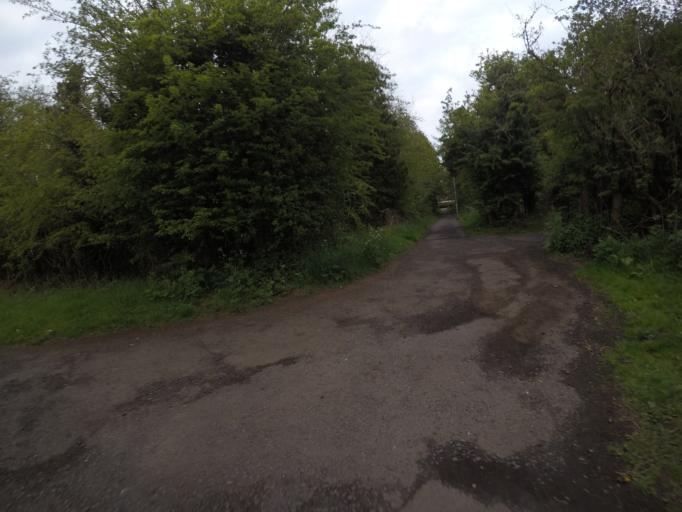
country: GB
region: Scotland
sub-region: North Ayrshire
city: Irvine
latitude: 55.6365
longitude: -4.6344
